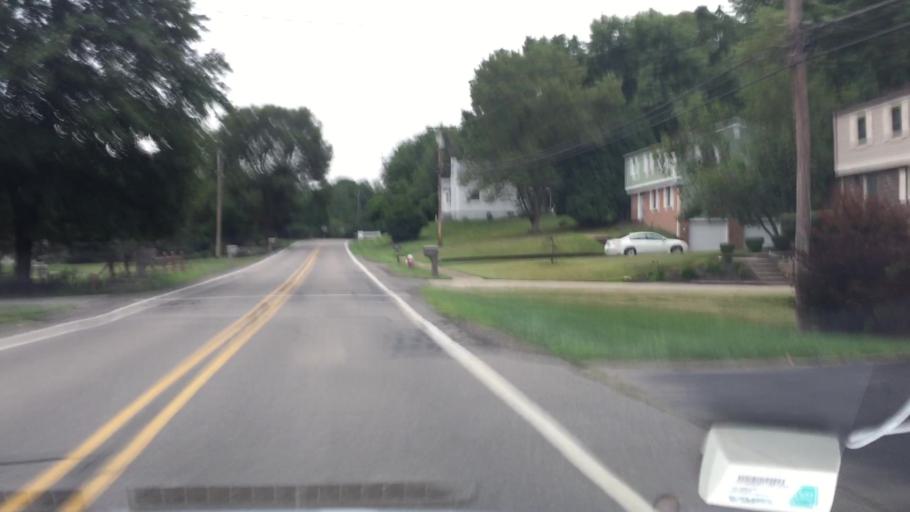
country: US
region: Pennsylvania
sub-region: Allegheny County
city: Franklin Park
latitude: 40.6068
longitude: -80.0757
